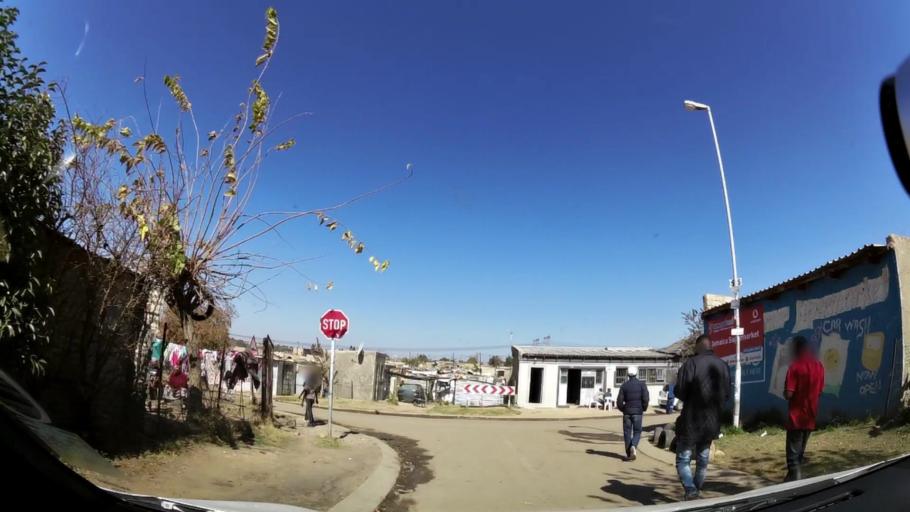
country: ZA
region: Gauteng
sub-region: City of Johannesburg Metropolitan Municipality
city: Diepsloot
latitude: -25.9178
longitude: 28.0888
